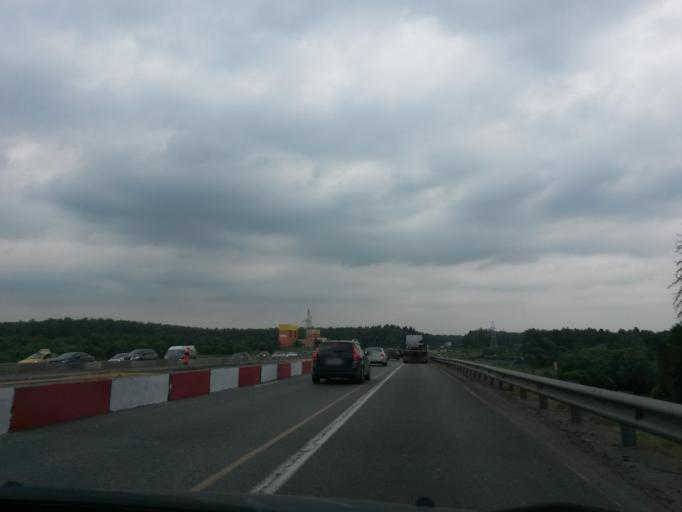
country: RU
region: Moskovskaya
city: Lyubuchany
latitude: 55.2321
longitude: 37.5290
